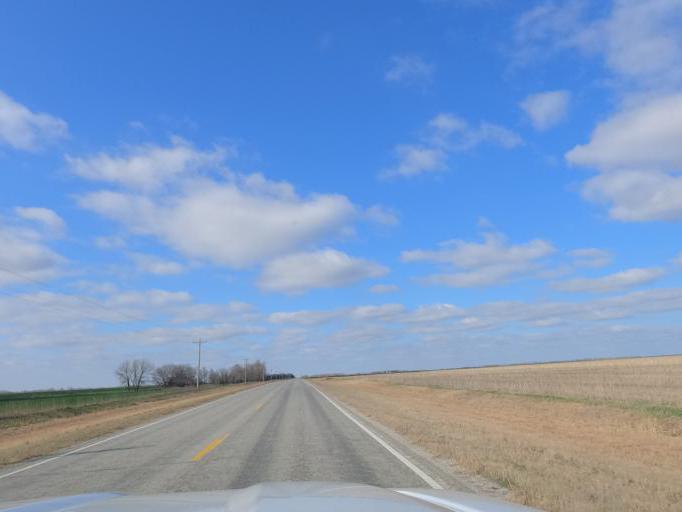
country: US
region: Kansas
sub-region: McPherson County
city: Inman
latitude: 38.1917
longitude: -97.8485
